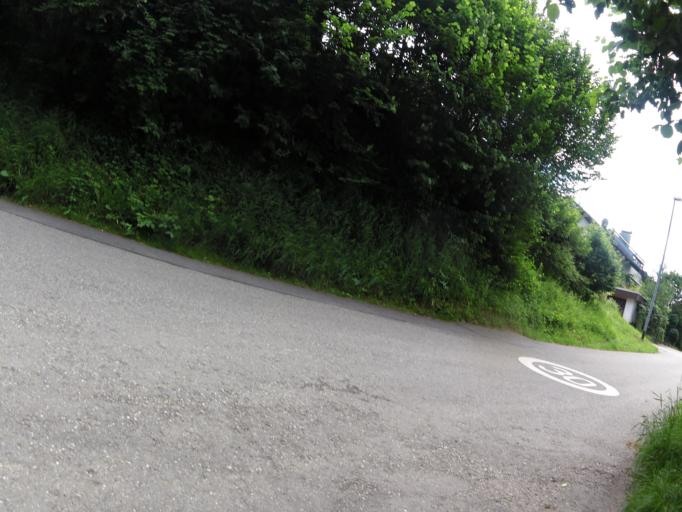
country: DE
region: Baden-Wuerttemberg
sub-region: Freiburg Region
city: Lahr
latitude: 48.3502
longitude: 7.8786
